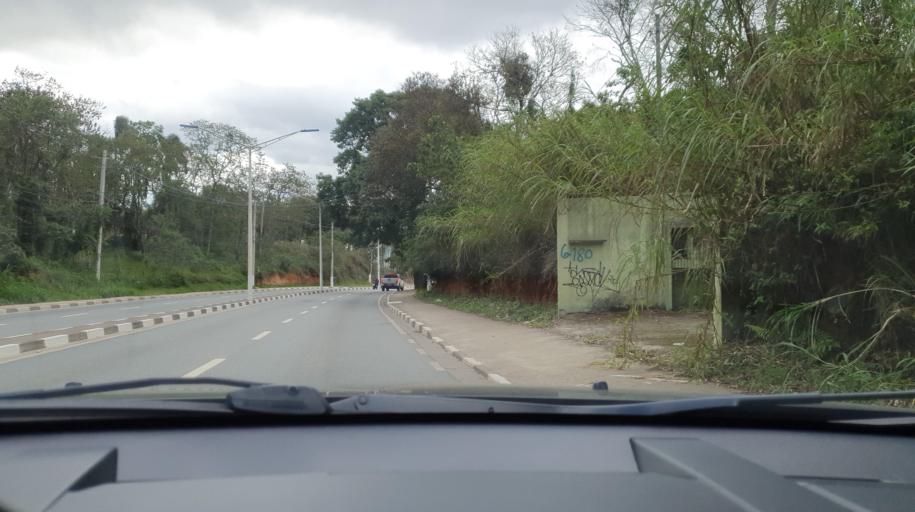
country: BR
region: Sao Paulo
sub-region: Vargem Grande Paulista
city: Vargem Grande Paulista
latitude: -23.6597
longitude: -47.0034
